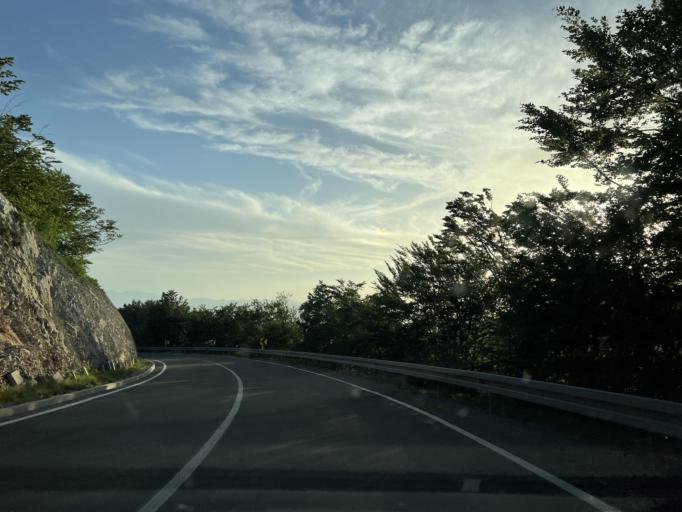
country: HR
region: Primorsko-Goranska
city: Podhum
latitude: 45.4021
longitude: 14.5477
